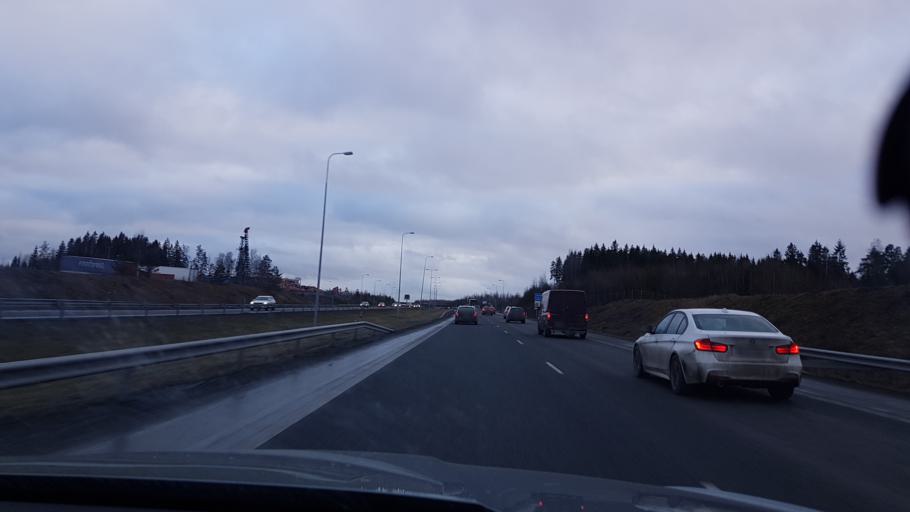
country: FI
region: Pirkanmaa
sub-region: Tampere
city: Lempaeaelae
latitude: 61.3746
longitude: 23.7899
